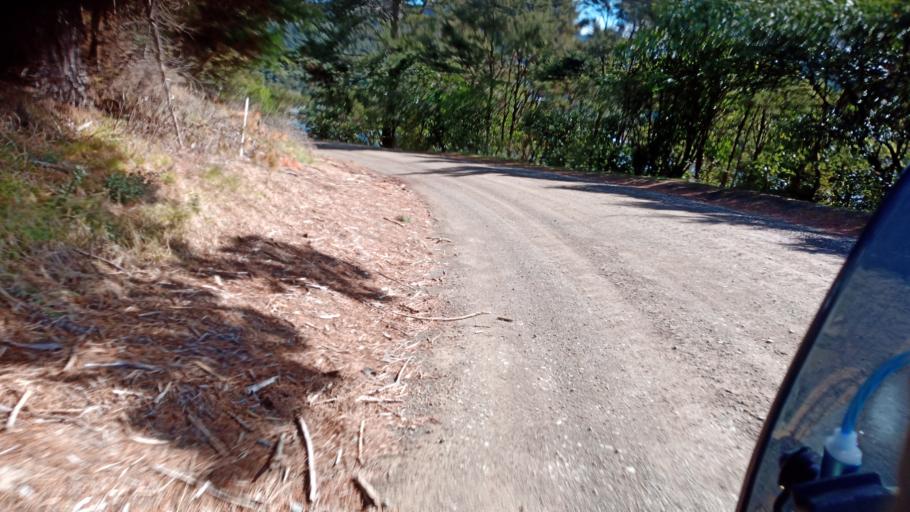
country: NZ
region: Hawke's Bay
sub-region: Wairoa District
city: Wairoa
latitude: -38.8134
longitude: 177.1541
